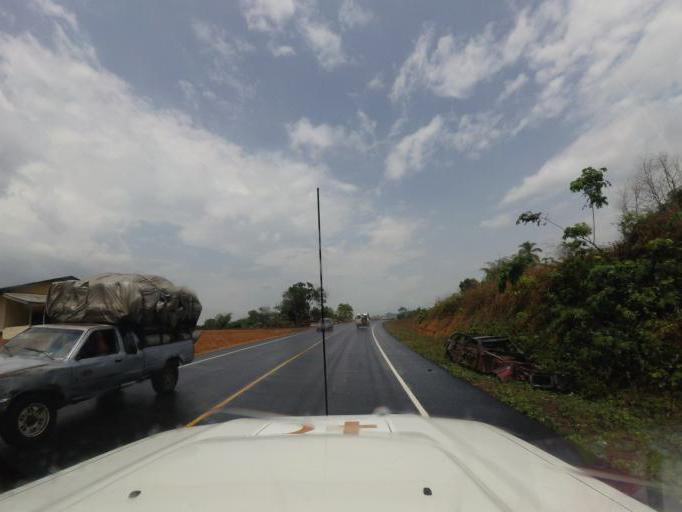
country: LR
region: Montserrado
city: Bensonville City
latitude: 6.4014
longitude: -10.5131
